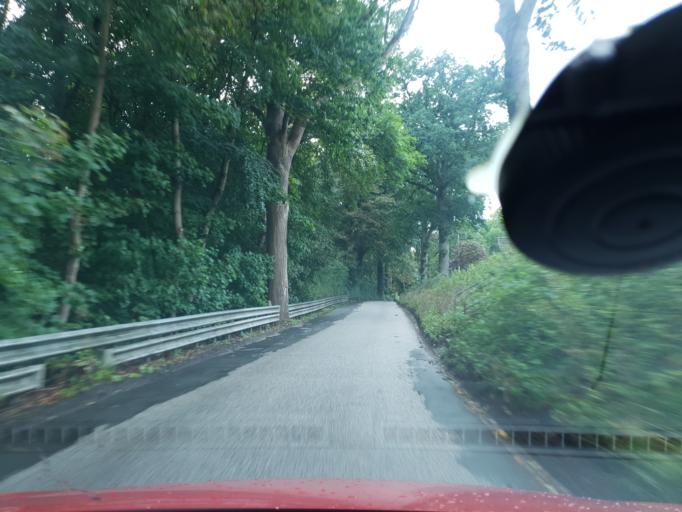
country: DE
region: Schleswig-Holstein
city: Molfsee
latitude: 54.2903
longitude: 10.0879
